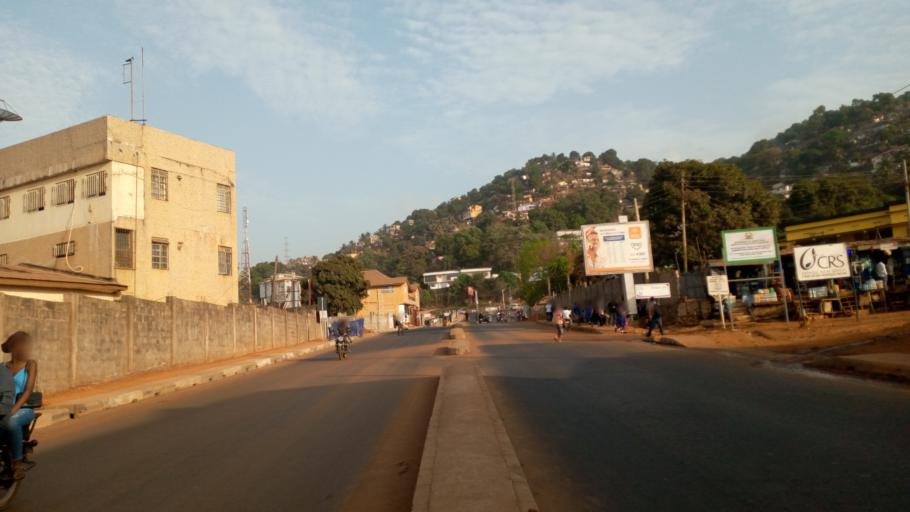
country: SL
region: Western Area
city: Freetown
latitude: 8.4709
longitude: -13.2468
